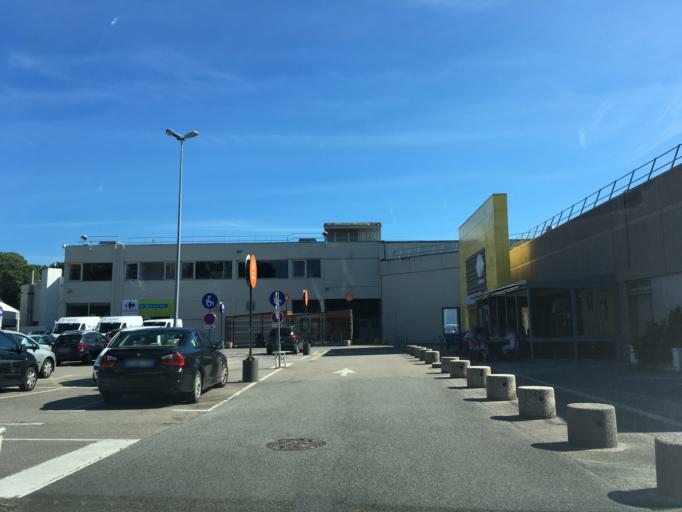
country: FR
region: Brittany
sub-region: Departement du Finistere
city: Quimper
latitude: 47.9843
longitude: -4.1074
